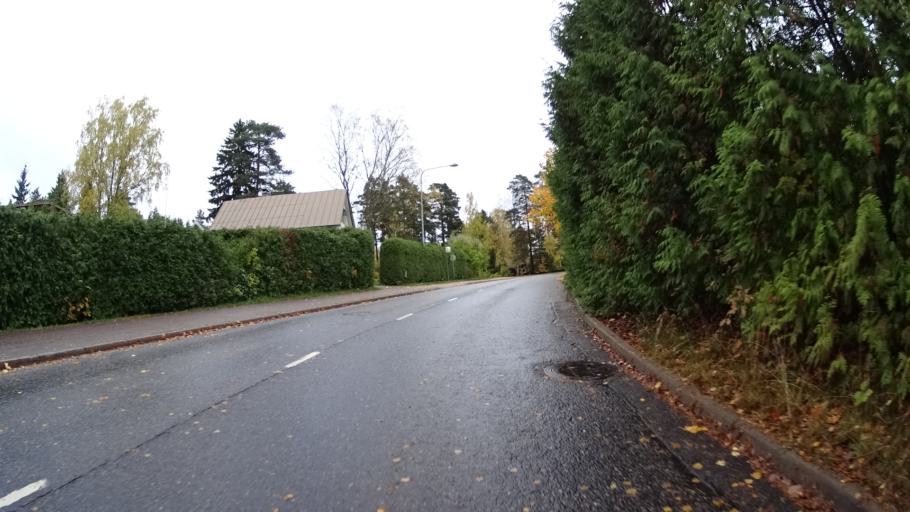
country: FI
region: Uusimaa
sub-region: Helsinki
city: Kilo
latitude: 60.2600
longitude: 24.8200
